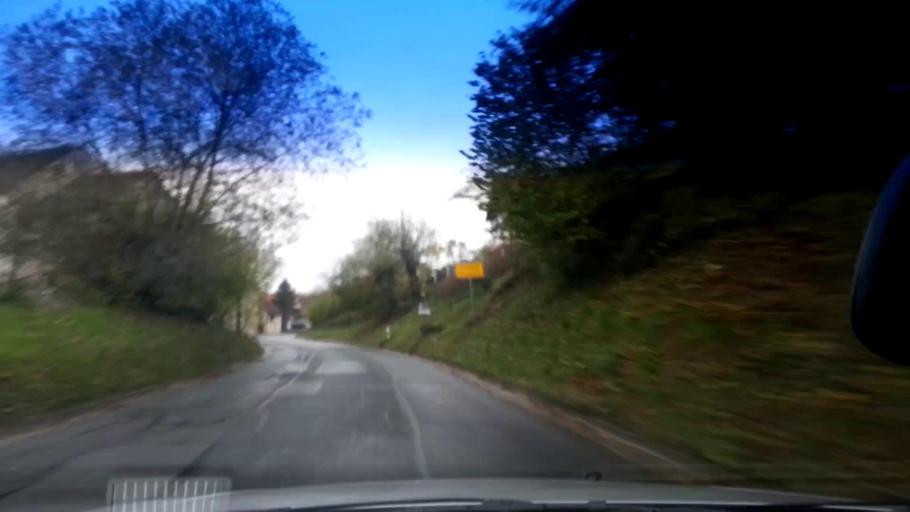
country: DE
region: Bavaria
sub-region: Upper Franconia
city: Wattendorf
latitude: 50.0132
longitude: 11.0754
